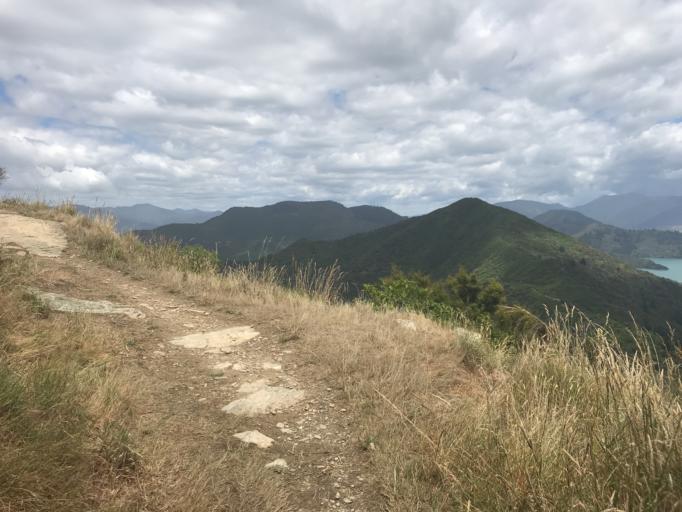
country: NZ
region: Marlborough
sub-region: Marlborough District
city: Picton
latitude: -41.2126
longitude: 174.0089
